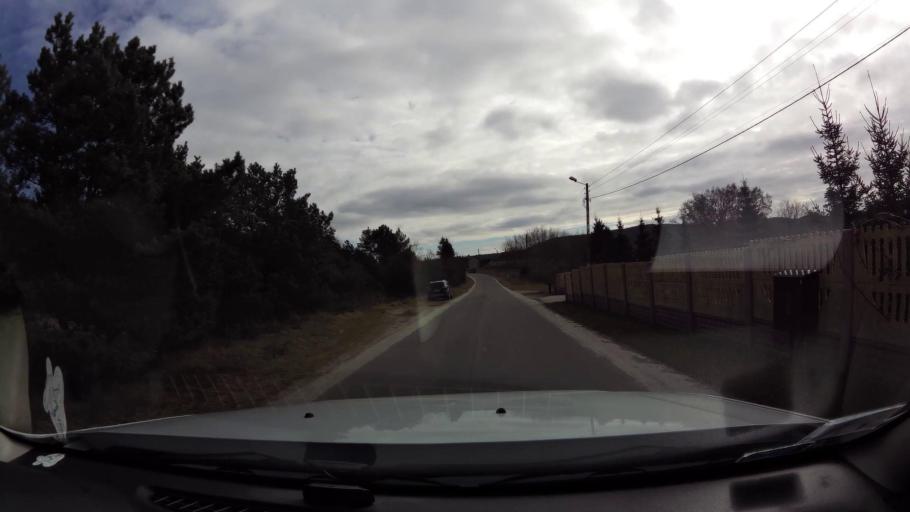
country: PL
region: West Pomeranian Voivodeship
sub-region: Powiat kamienski
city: Miedzyzdroje
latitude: 53.8884
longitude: 14.4395
